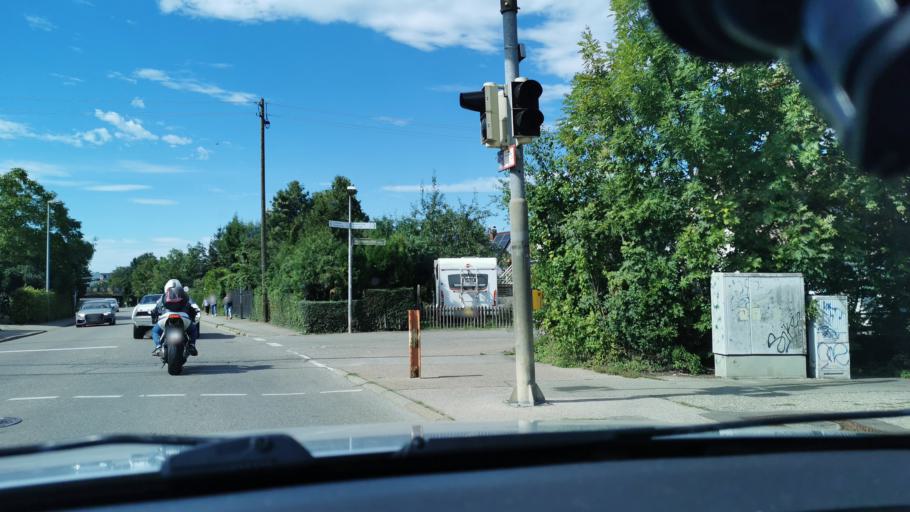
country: DE
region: Baden-Wuerttemberg
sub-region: Regierungsbezirk Stuttgart
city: Kirchheim unter Teck
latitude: 48.6377
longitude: 9.4639
